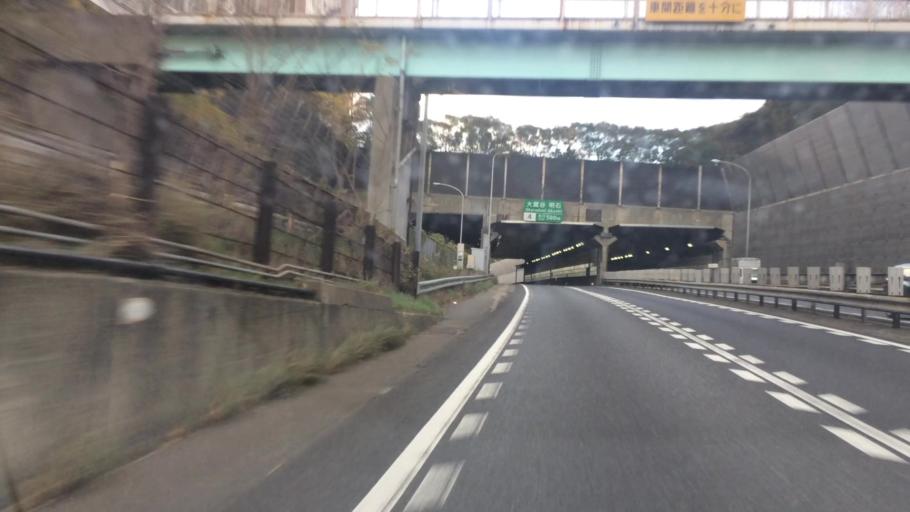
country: JP
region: Hyogo
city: Akashi
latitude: 34.6569
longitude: 135.0337
